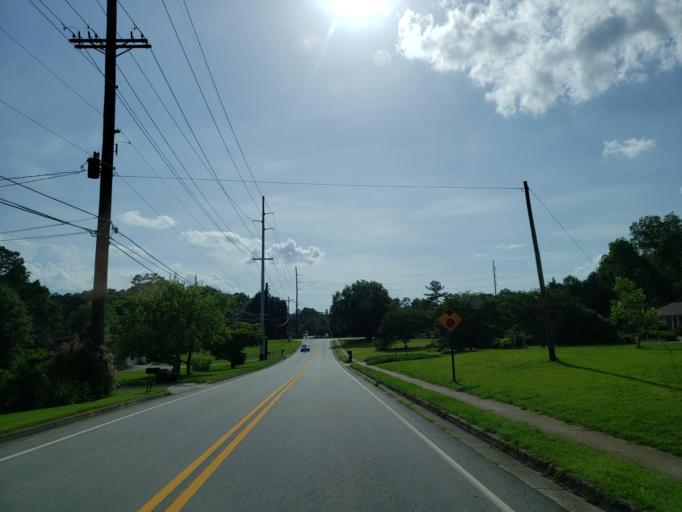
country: US
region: Georgia
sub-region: Cobb County
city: Powder Springs
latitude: 33.8752
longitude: -84.6827
